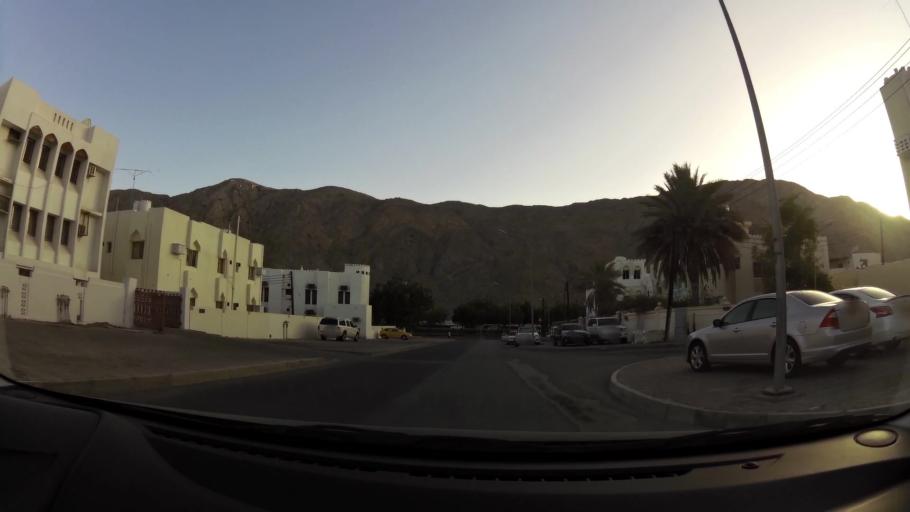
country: OM
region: Muhafazat Masqat
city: Muscat
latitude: 23.5741
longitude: 58.5685
